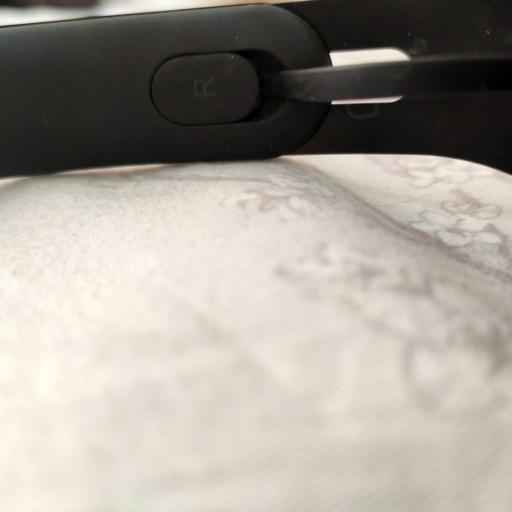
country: RU
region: Moskovskaya
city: Povedniki
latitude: 55.9314
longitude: 37.6438
